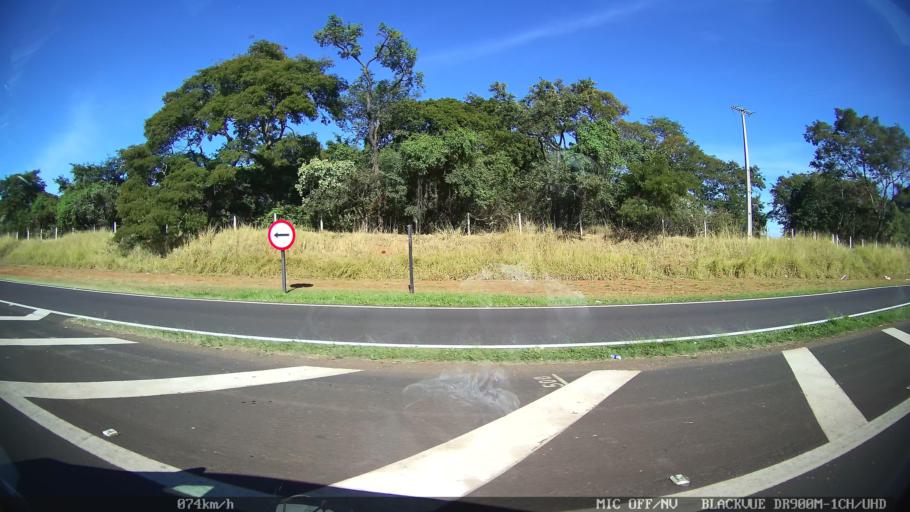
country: BR
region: Sao Paulo
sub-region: Franca
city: Franca
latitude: -20.5632
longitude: -47.4118
